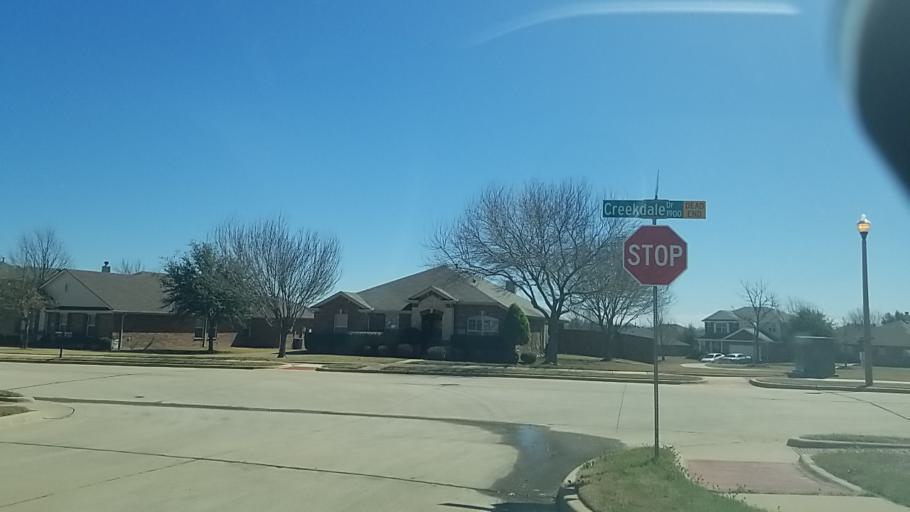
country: US
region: Texas
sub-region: Denton County
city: Corinth
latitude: 33.1549
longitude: -97.1128
